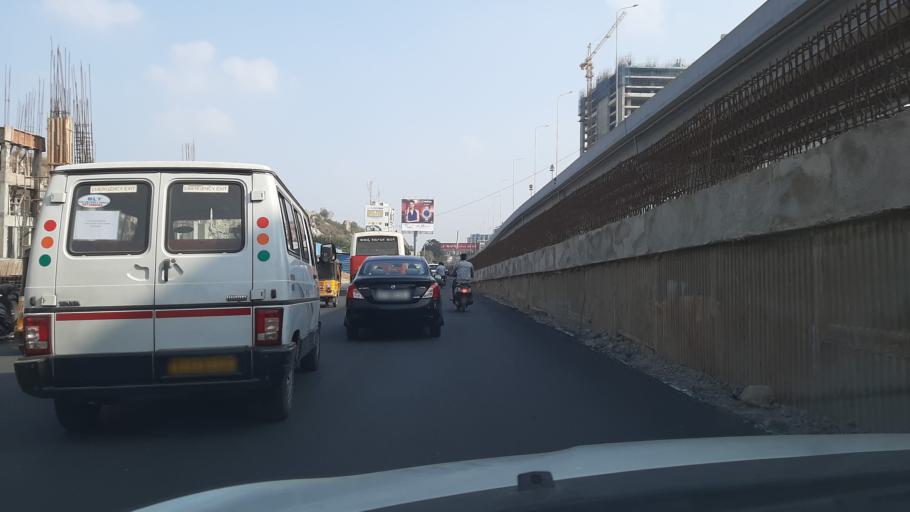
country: IN
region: Telangana
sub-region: Rangareddi
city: Kukatpalli
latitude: 17.4277
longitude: 78.3760
